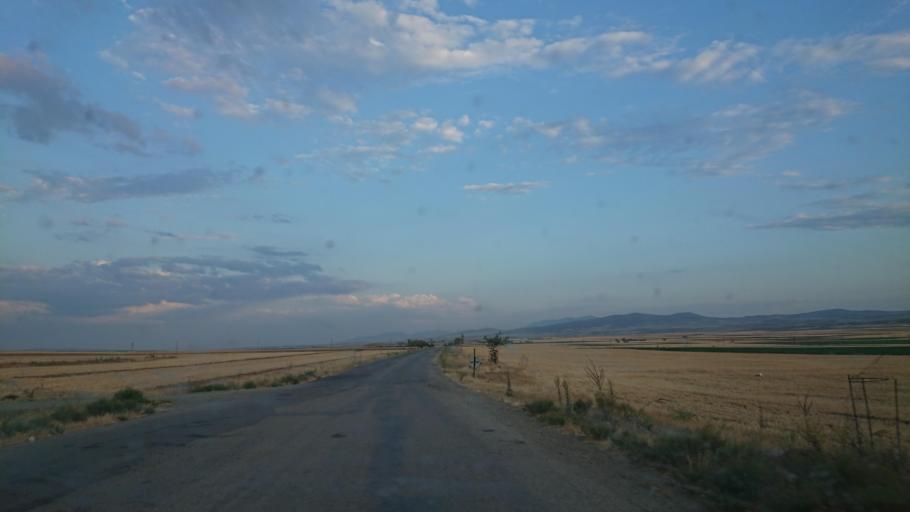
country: TR
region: Aksaray
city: Agacoren
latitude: 38.9192
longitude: 34.0360
